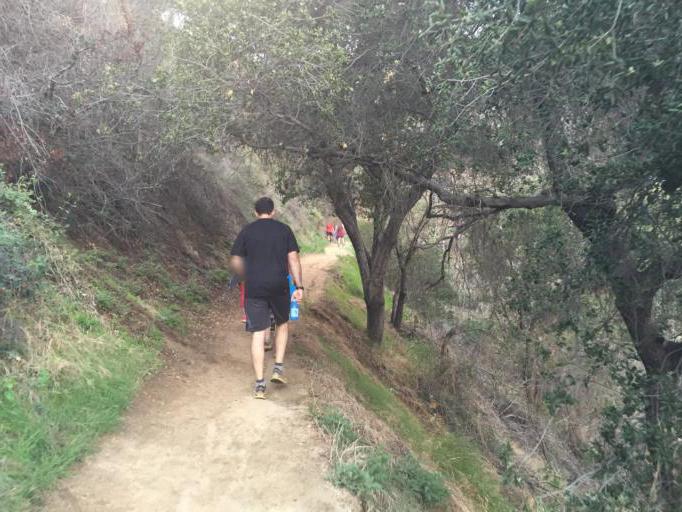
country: US
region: California
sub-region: Los Angeles County
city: Sierra Madre
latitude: 34.1737
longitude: -118.0475
